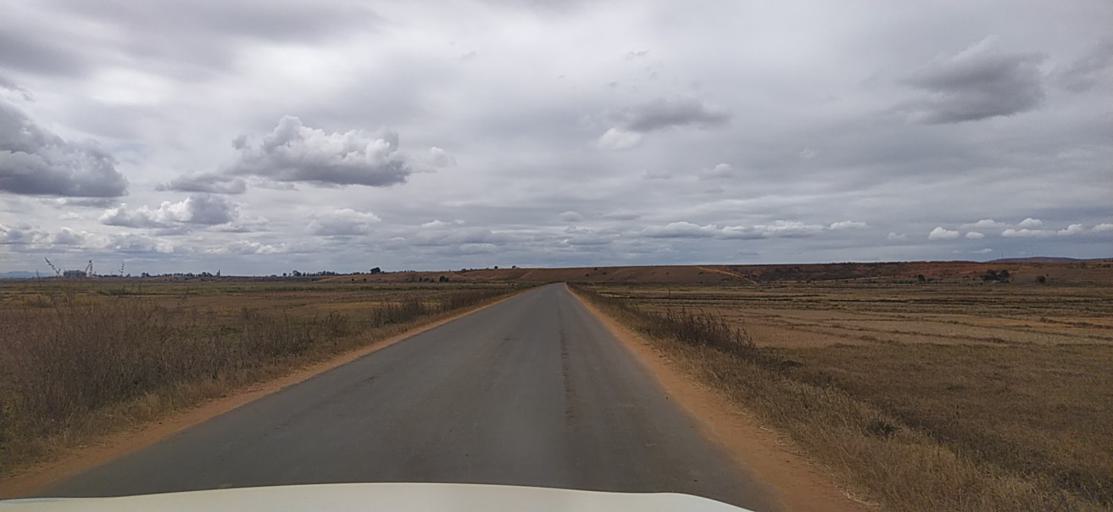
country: MG
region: Alaotra Mangoro
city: Ambatondrazaka
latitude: -17.9203
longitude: 48.2578
